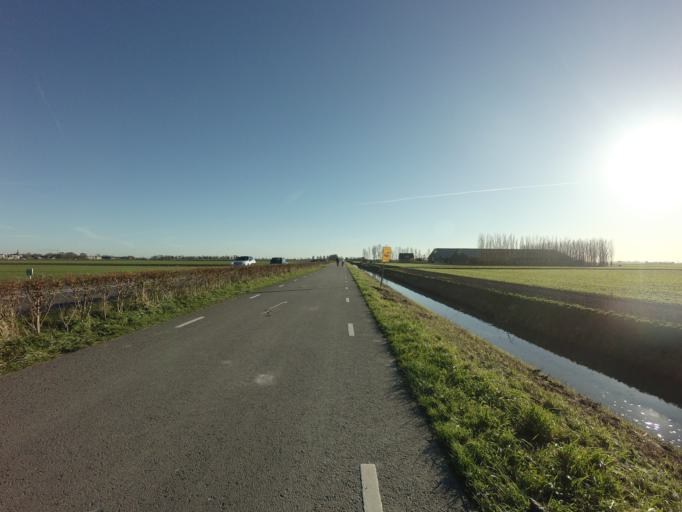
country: NL
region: South Holland
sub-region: Gemeente Nieuwkoop
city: Nieuwkoop
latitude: 52.1848
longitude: 4.7643
